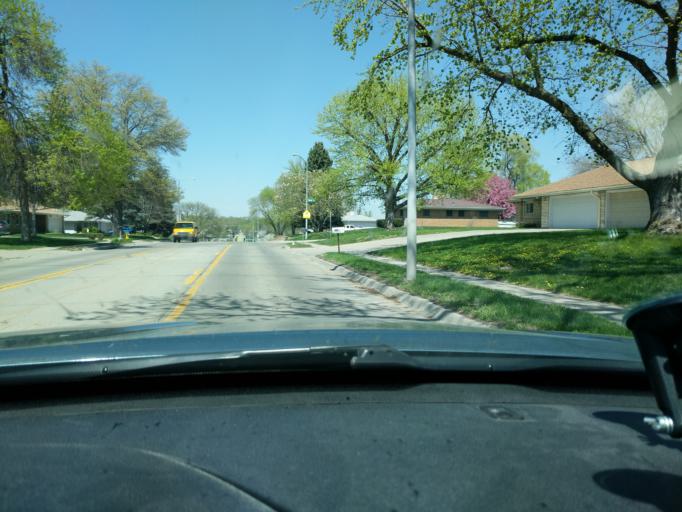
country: US
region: Nebraska
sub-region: Douglas County
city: Ralston
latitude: 41.2301
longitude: -96.0815
